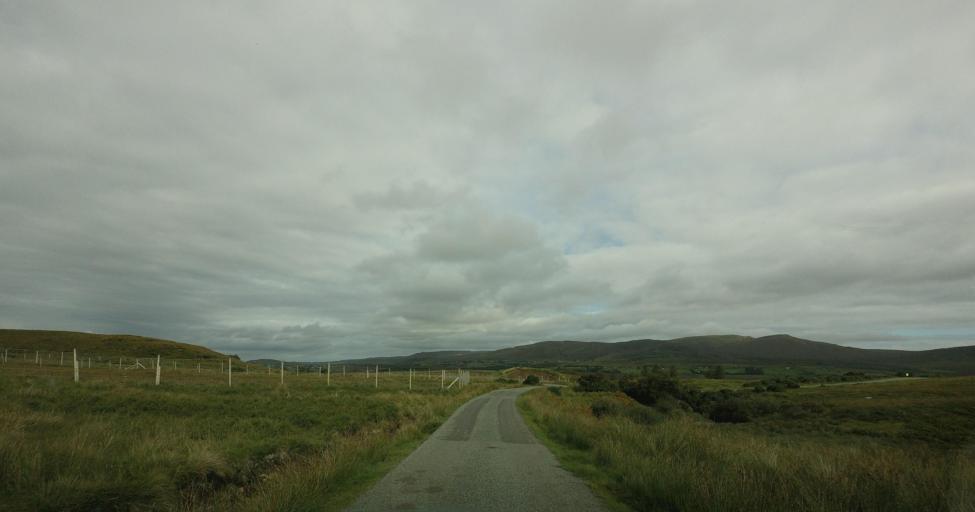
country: GB
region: Scotland
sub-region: Highland
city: Isle of Skye
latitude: 57.4204
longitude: -6.2577
